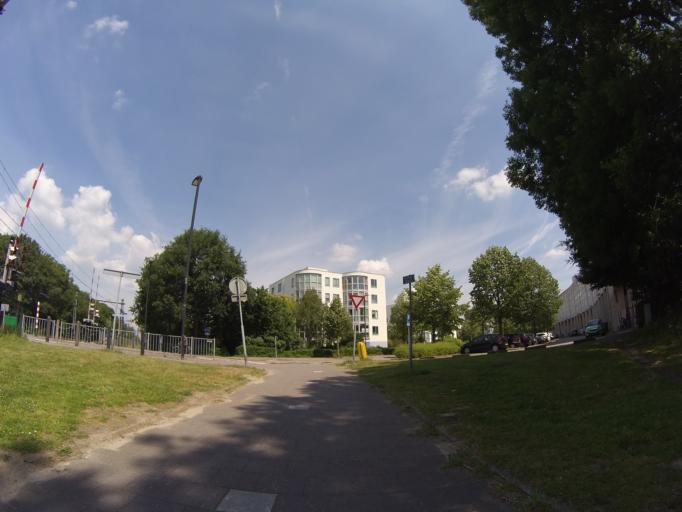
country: NL
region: Utrecht
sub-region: Gemeente Utrecht
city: Utrecht
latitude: 52.1060
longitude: 5.1411
